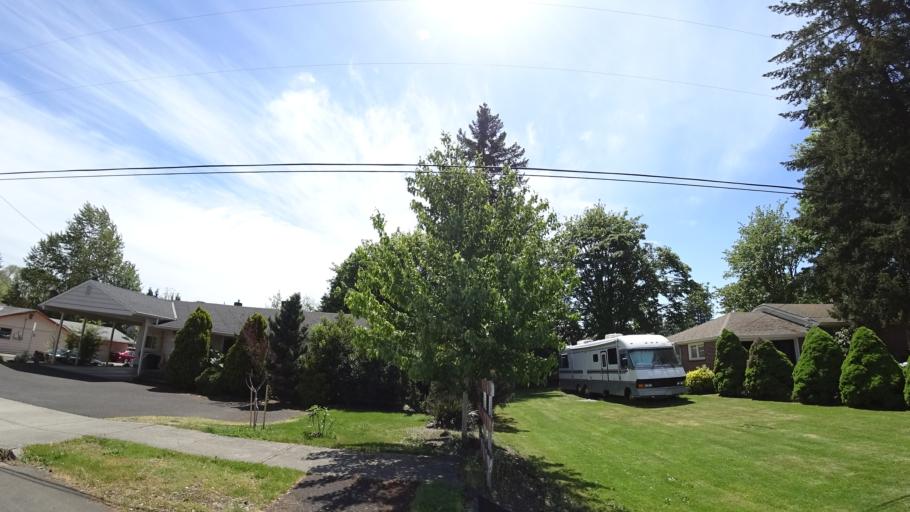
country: US
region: Oregon
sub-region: Washington County
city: Aloha
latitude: 45.4869
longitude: -122.8569
